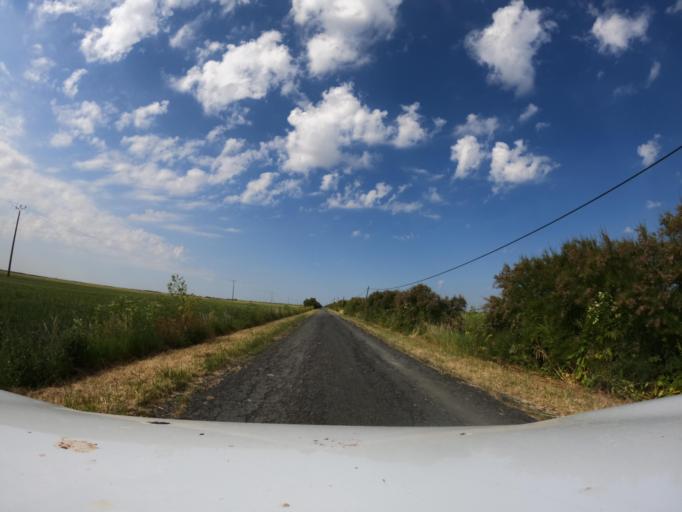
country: FR
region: Pays de la Loire
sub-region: Departement de la Vendee
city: Champagne-les-Marais
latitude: 46.3349
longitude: -1.1372
